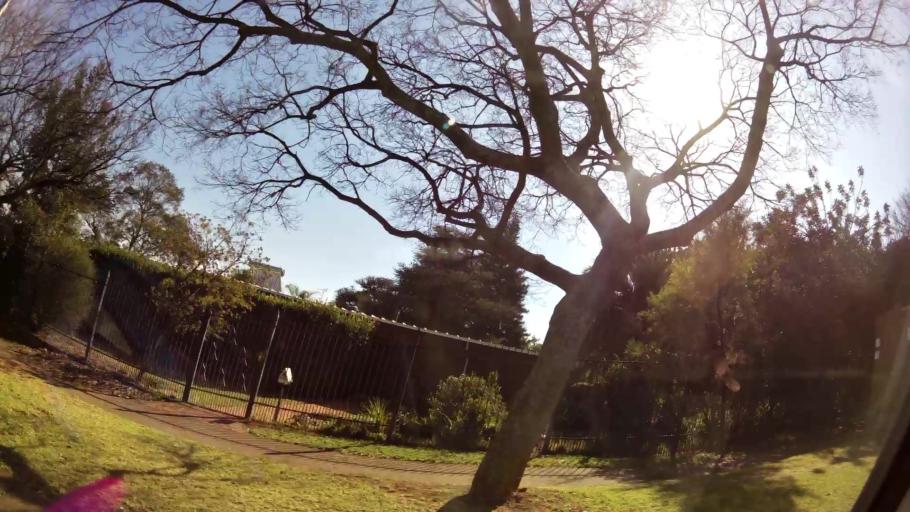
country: ZA
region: Gauteng
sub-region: City of Tshwane Metropolitan Municipality
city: Pretoria
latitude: -25.8003
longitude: 28.2377
